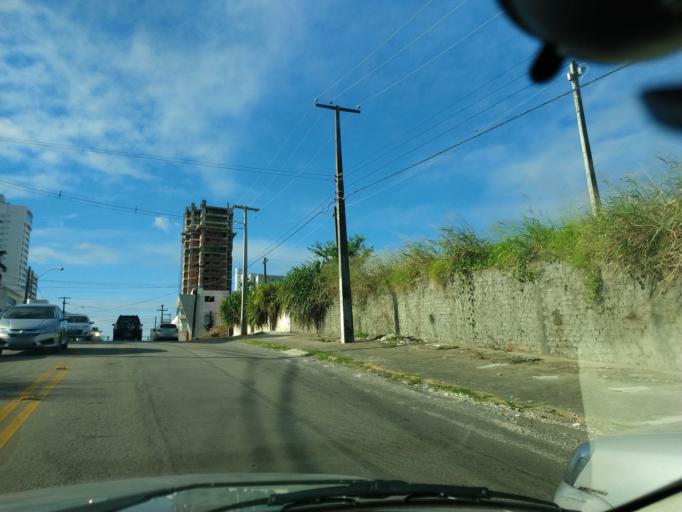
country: BR
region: Rio Grande do Norte
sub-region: Natal
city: Natal
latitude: -5.8309
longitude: -35.2227
